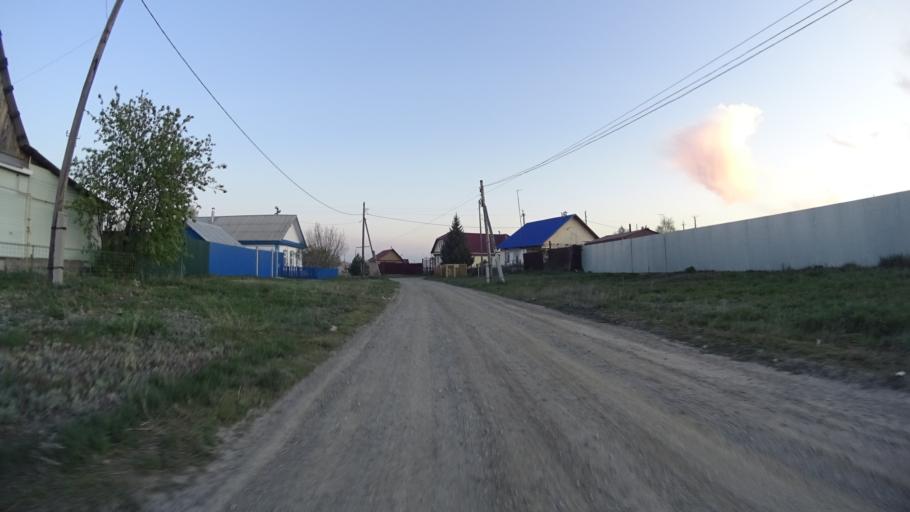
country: RU
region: Chelyabinsk
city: Bobrovka
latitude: 54.0436
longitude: 61.7446
